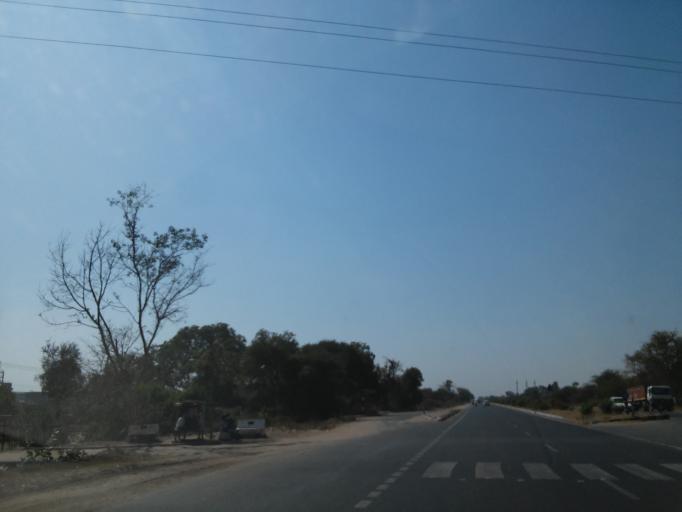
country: IN
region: Gujarat
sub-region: Sabar Kantha
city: Himatnagar
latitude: 23.5133
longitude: 72.9308
